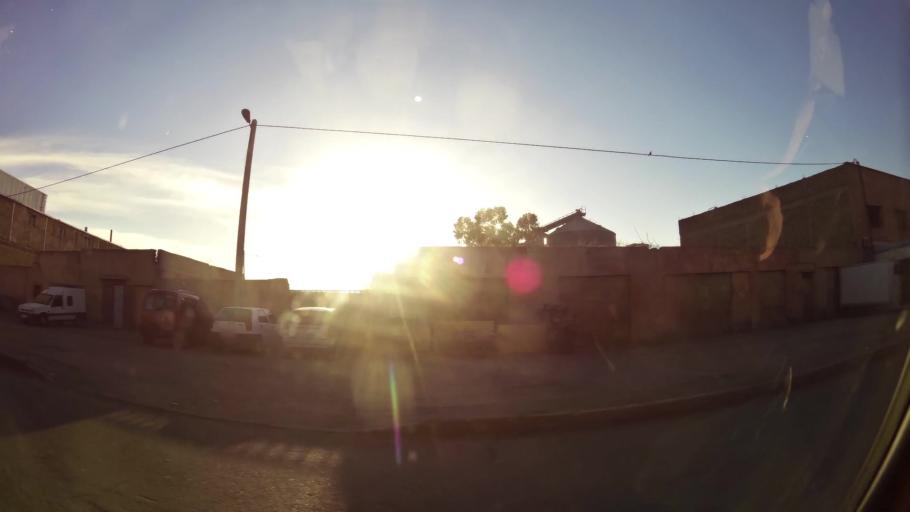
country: MA
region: Marrakech-Tensift-Al Haouz
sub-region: Marrakech
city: Marrakesh
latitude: 31.6258
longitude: -8.0430
